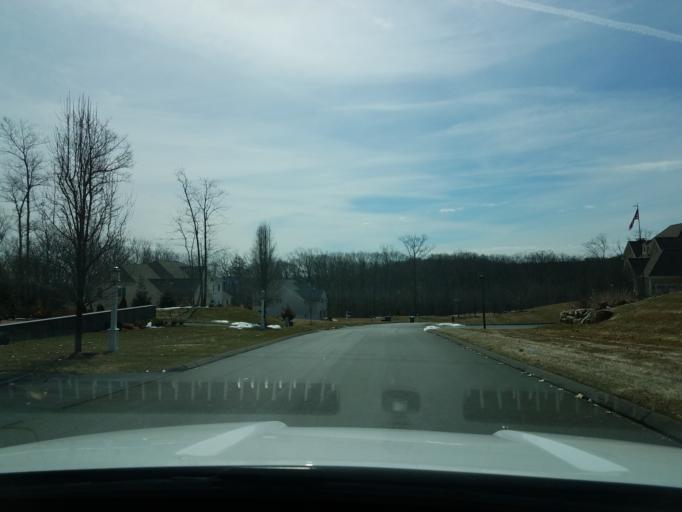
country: US
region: Connecticut
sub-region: Hartford County
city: Collinsville
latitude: 41.8040
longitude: -72.9001
